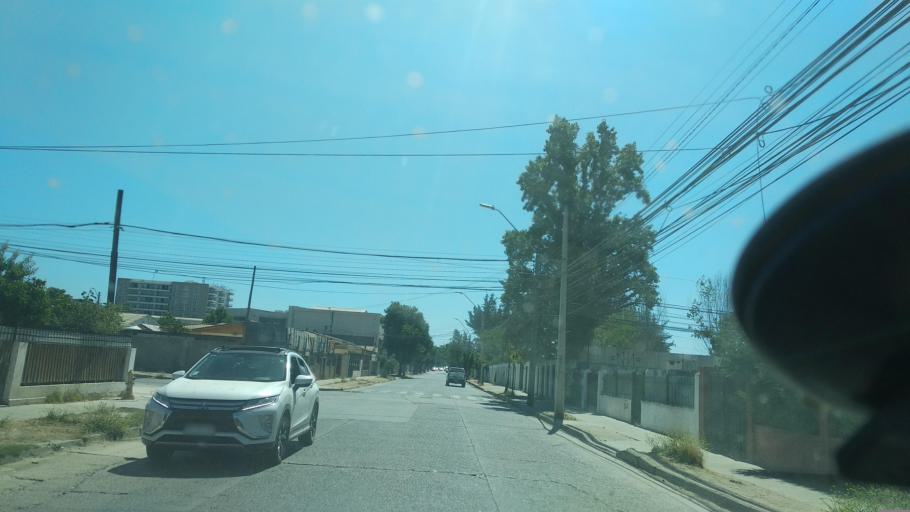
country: CL
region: Valparaiso
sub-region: Provincia de Marga Marga
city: Villa Alemana
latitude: -33.0460
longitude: -71.3628
